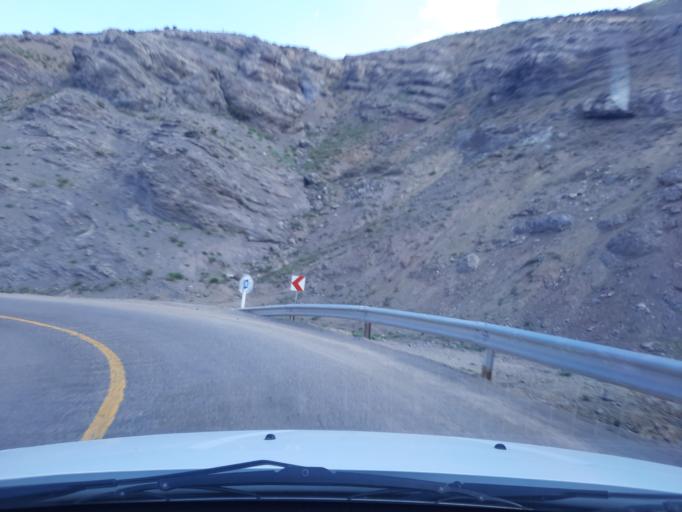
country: IR
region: Qazvin
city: Qazvin
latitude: 36.3976
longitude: 50.2178
